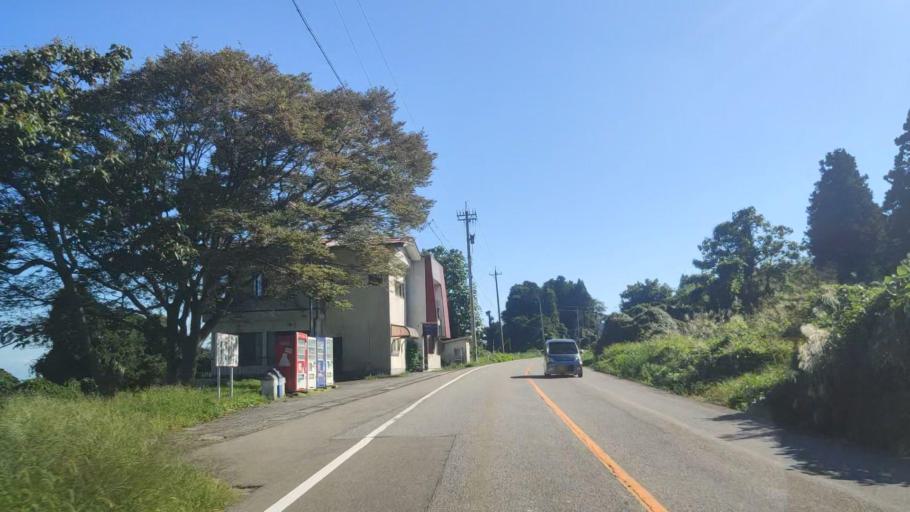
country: JP
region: Ishikawa
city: Nanao
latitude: 37.2701
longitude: 137.0949
